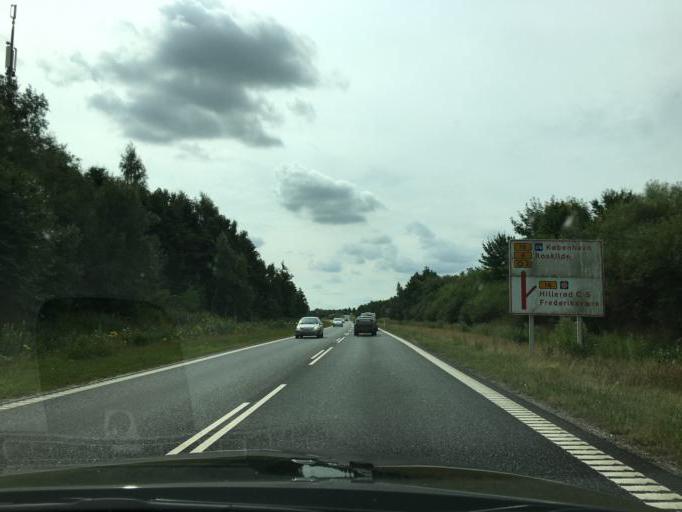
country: DK
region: Capital Region
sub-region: Hillerod Kommune
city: Hillerod
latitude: 55.9422
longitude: 12.2448
